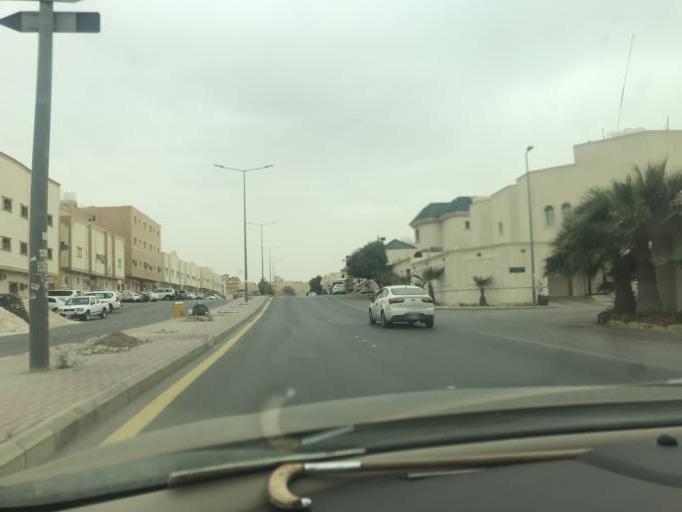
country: SA
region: Ar Riyad
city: Riyadh
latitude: 24.7375
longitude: 46.7563
